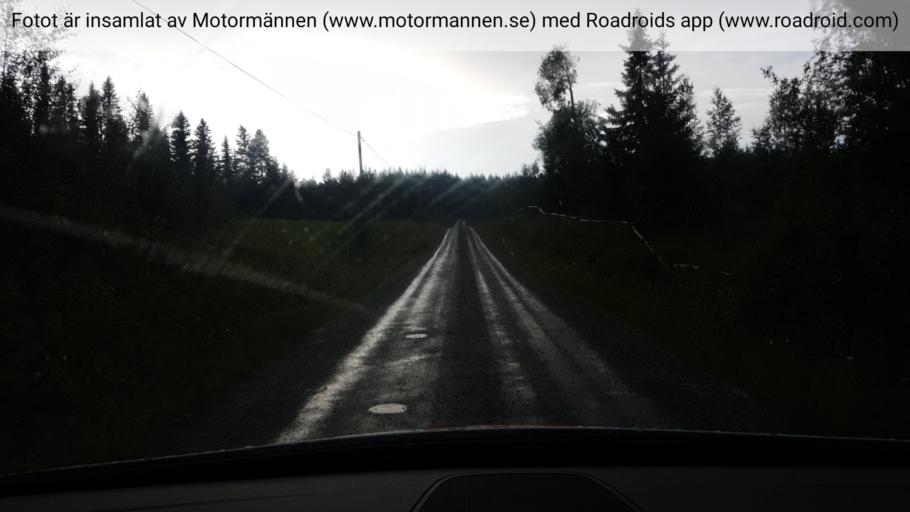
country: SE
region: Jaemtland
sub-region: OEstersunds Kommun
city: Brunflo
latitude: 63.0460
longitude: 14.7157
